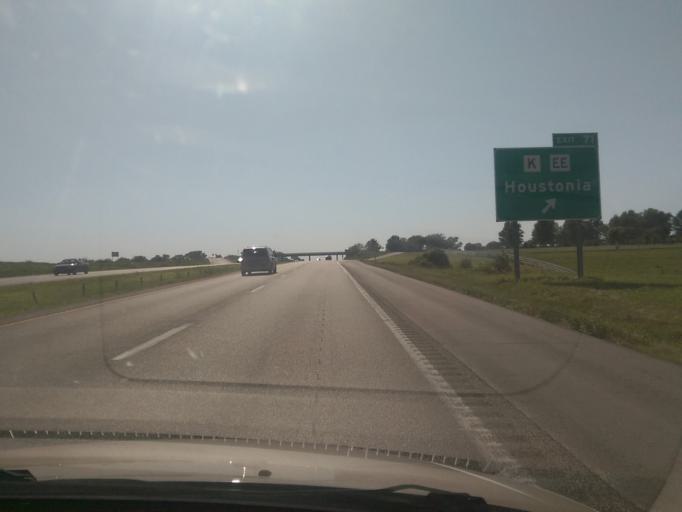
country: US
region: Missouri
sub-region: Saline County
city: Sweet Springs
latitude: 38.9735
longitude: -93.3271
